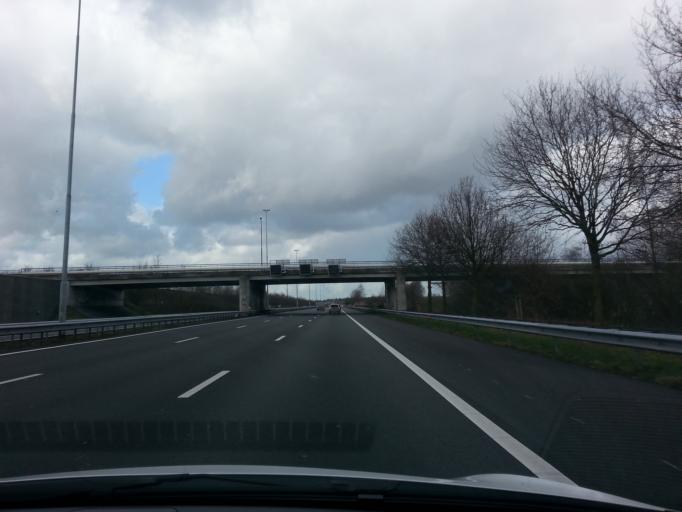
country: NL
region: North Brabant
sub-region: Gemeente Boxtel
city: Boxtel
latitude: 51.5957
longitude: 5.3427
